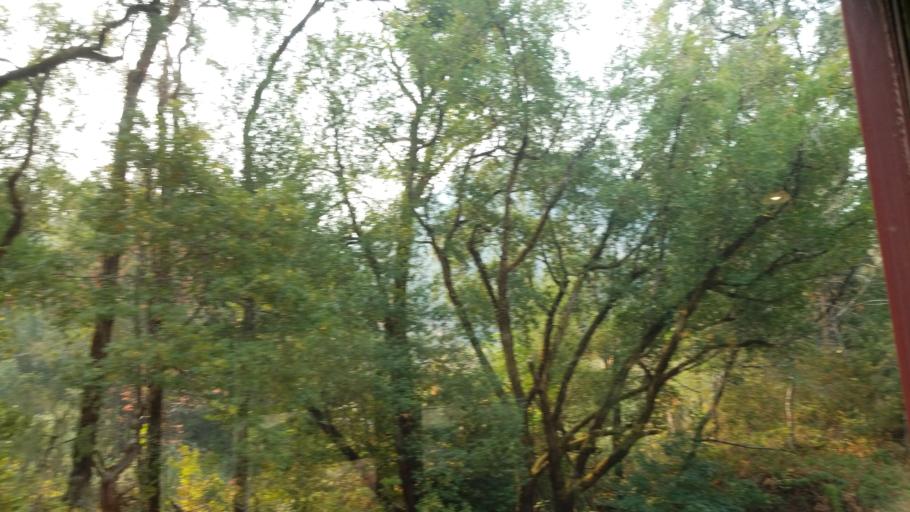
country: US
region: California
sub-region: Mendocino County
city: Willits
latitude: 39.4075
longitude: -123.3813
